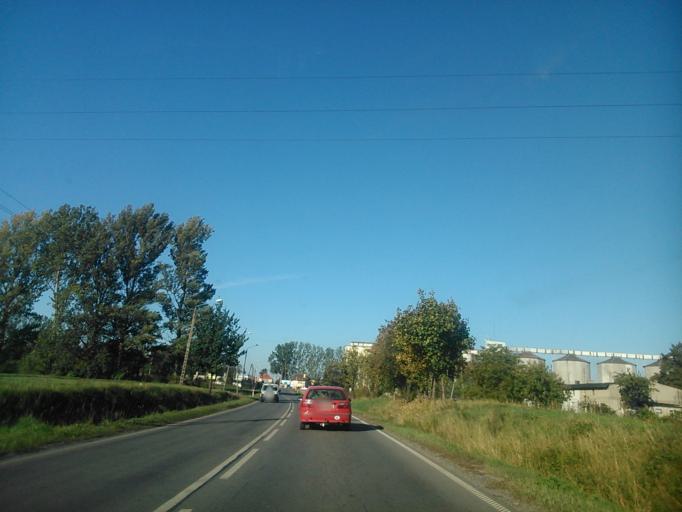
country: PL
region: Kujawsko-Pomorskie
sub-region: Powiat wabrzeski
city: Wabrzezno
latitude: 53.2665
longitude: 18.9881
